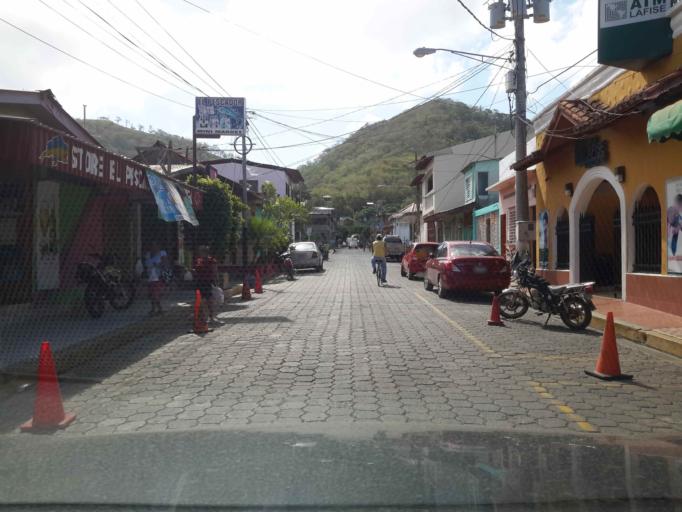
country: NI
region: Rivas
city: San Juan del Sur
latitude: 11.2532
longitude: -85.8705
